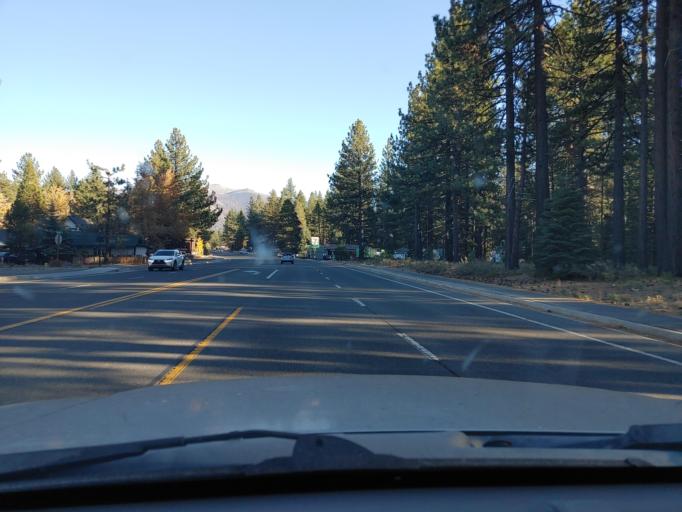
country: US
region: California
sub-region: El Dorado County
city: South Lake Tahoe
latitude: 38.9189
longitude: -120.0125
